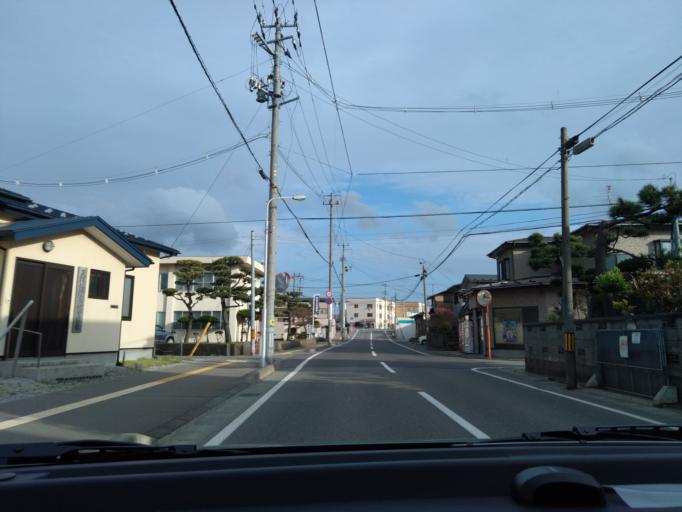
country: JP
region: Akita
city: Akita Shi
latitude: 39.7565
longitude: 140.0741
